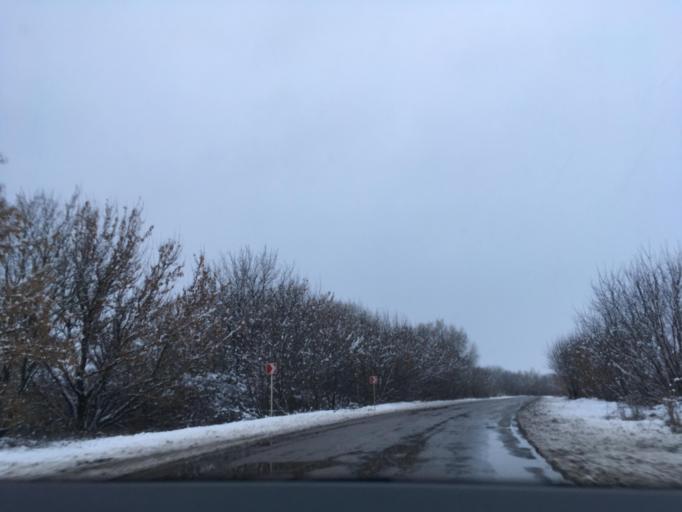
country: RU
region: Voronezj
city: Mitrofanovka
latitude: 50.1316
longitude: 39.9955
